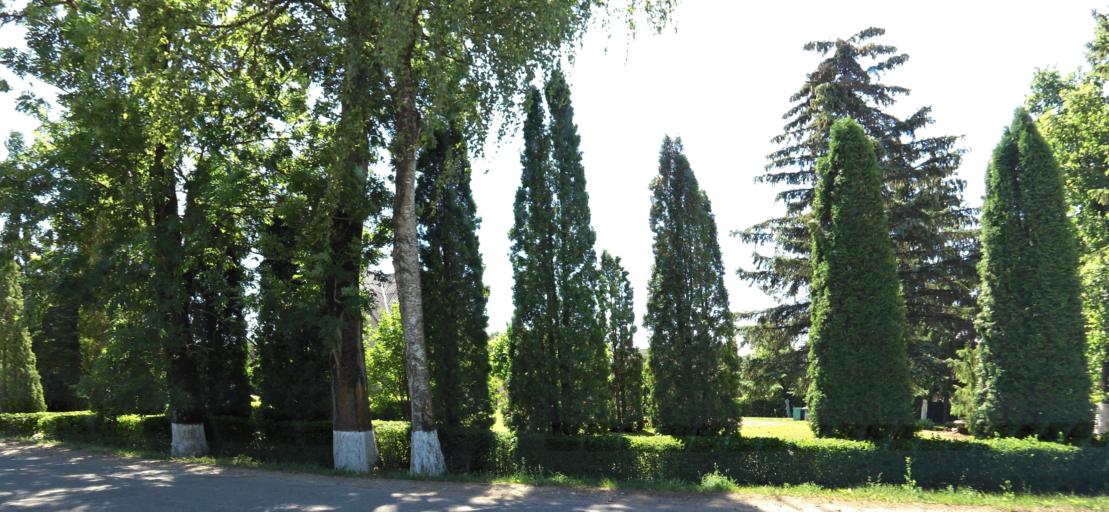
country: LT
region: Panevezys
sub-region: Birzai
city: Birzai
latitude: 56.2535
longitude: 24.5396
